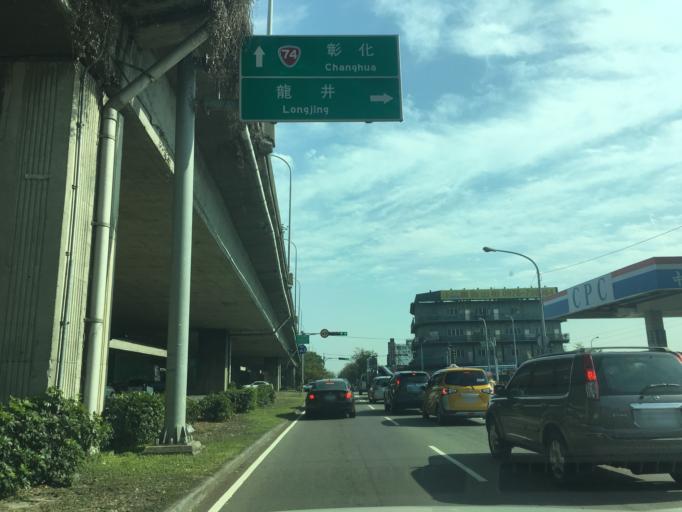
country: TW
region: Taiwan
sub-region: Taichung City
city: Taichung
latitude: 24.1461
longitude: 120.6229
